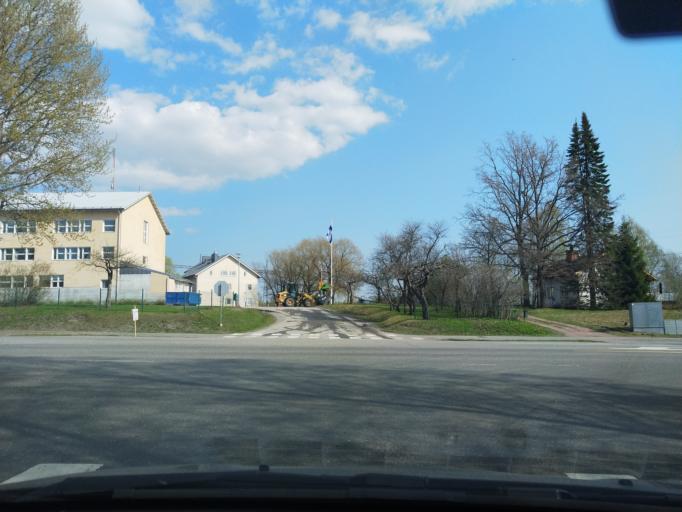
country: FI
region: Uusimaa
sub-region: Helsinki
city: Lohja
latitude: 60.1803
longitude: 23.9911
